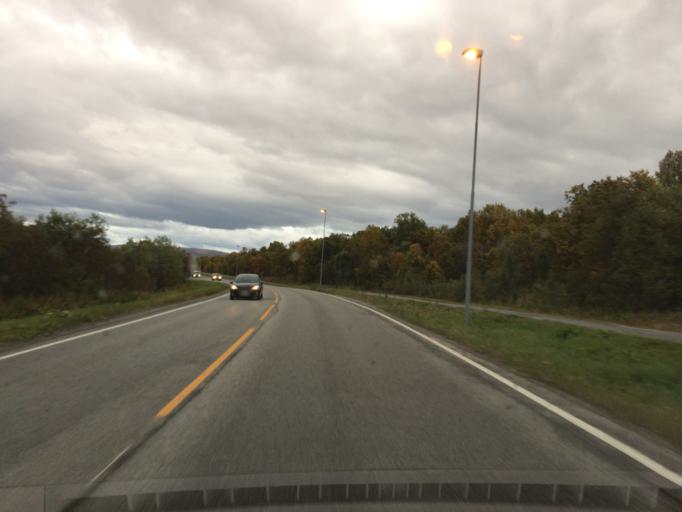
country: NO
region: Troms
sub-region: Tromso
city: Tromso
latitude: 69.6849
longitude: 18.9075
